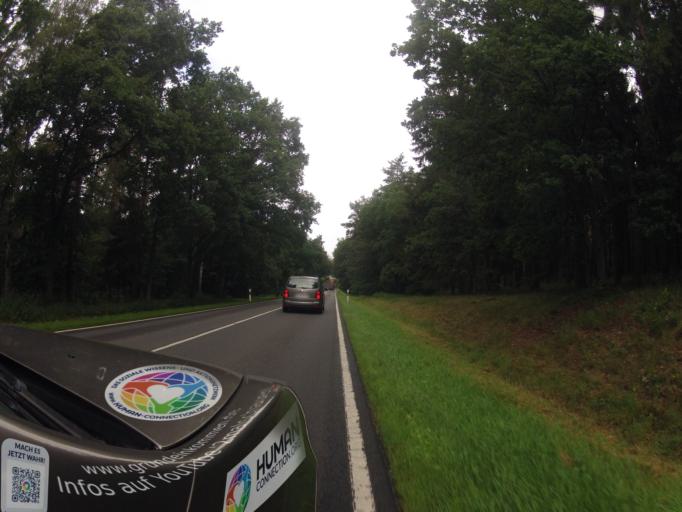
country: DE
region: Mecklenburg-Vorpommern
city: Lassan
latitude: 53.8933
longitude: 13.7881
